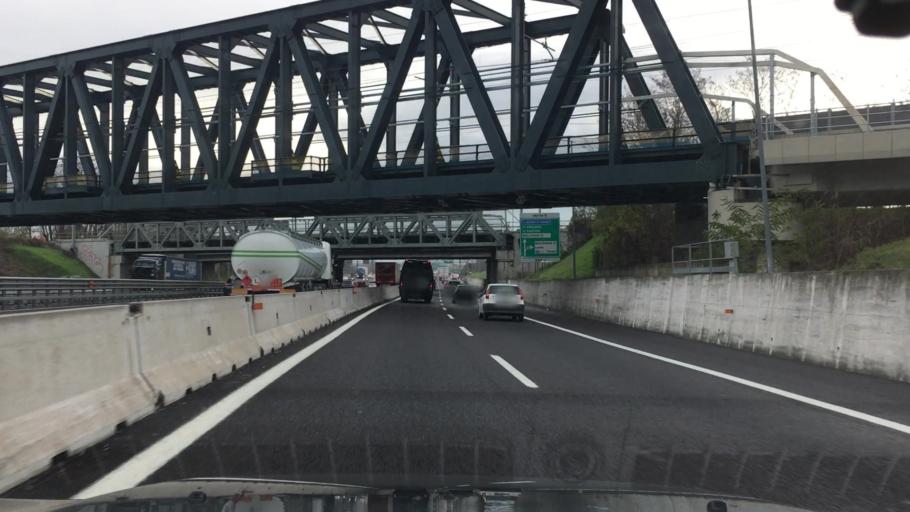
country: IT
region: Emilia-Romagna
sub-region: Provincia di Bologna
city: Trebbo
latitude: 44.5319
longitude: 11.3336
